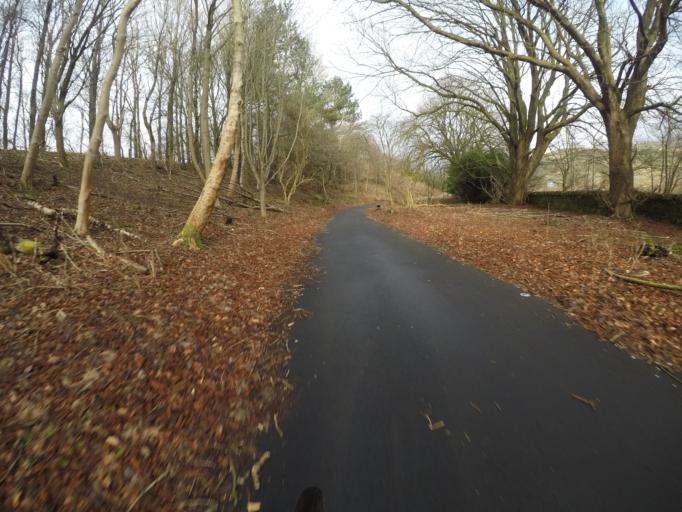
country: GB
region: Scotland
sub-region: North Ayrshire
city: Fairlie
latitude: 55.7395
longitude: -4.8615
